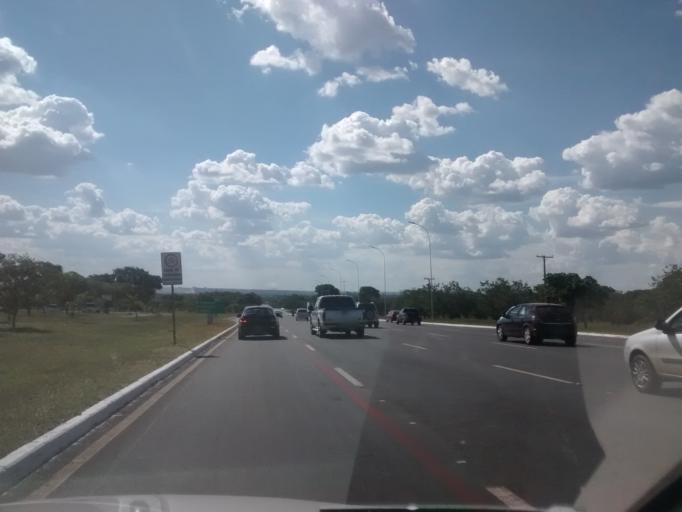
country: BR
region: Federal District
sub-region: Brasilia
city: Brasilia
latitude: -15.7803
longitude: -47.9229
